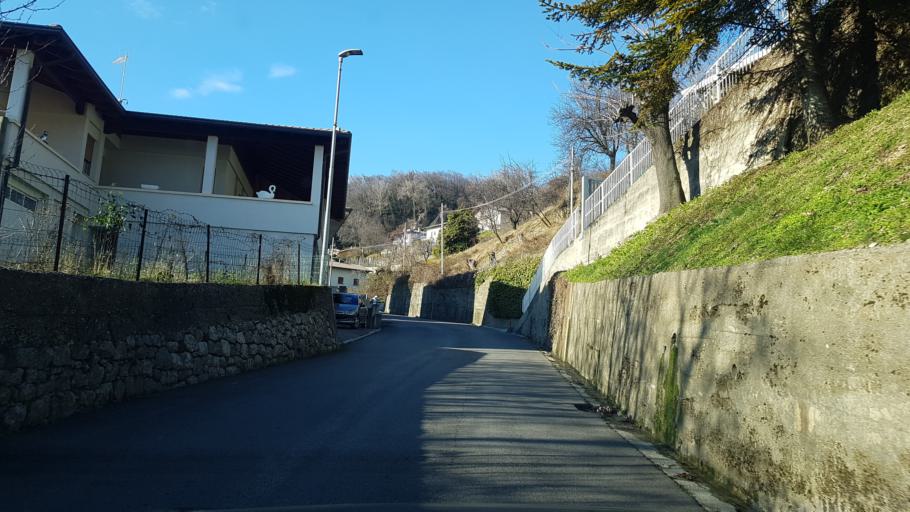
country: IT
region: Friuli Venezia Giulia
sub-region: Provincia di Udine
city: Forgaria nel Friuli
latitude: 46.2241
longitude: 12.9742
